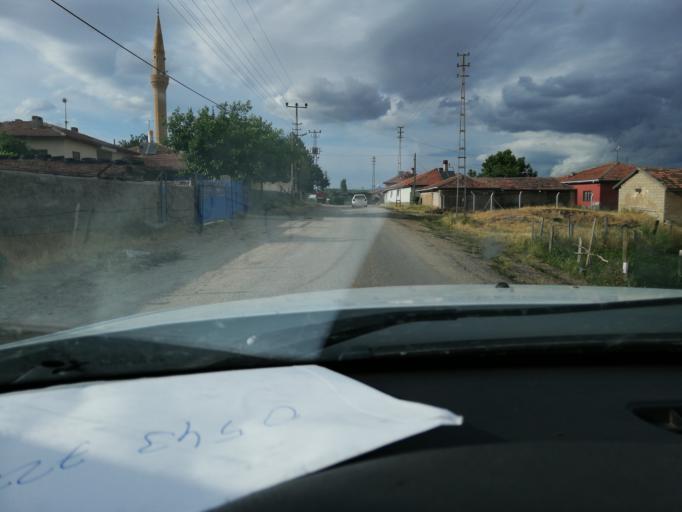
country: TR
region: Kirsehir
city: Kirsehir
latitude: 39.0275
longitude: 34.1266
